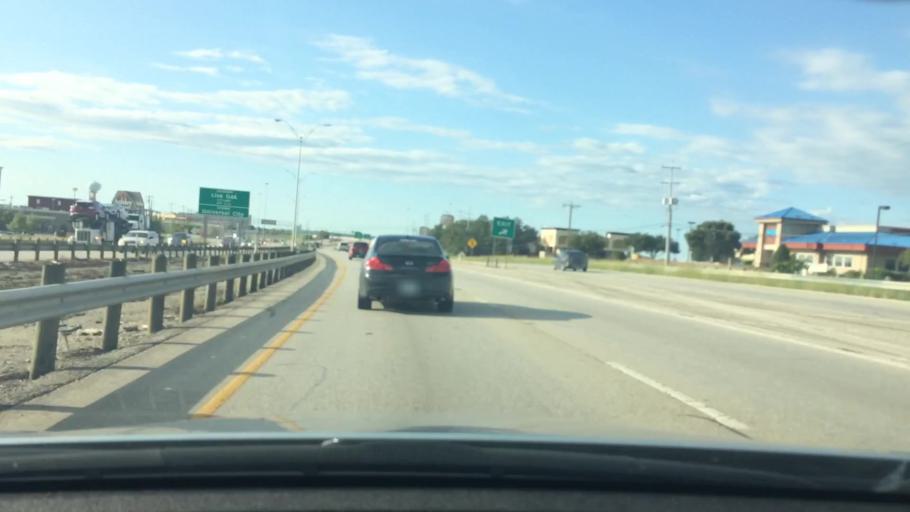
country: US
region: Texas
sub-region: Bexar County
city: Live Oak
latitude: 29.5619
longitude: -98.3280
